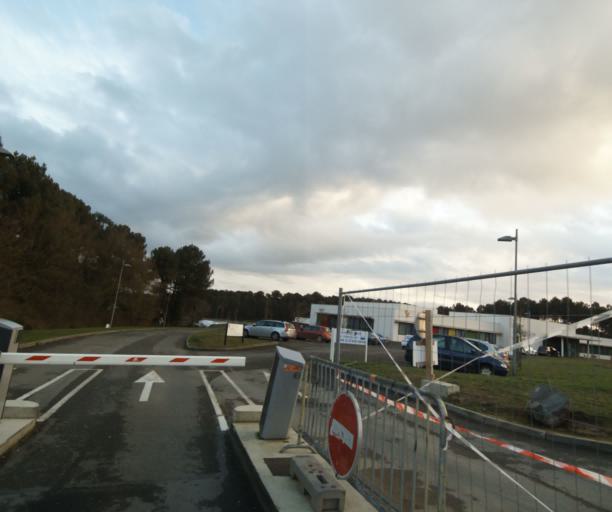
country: FR
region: Pays de la Loire
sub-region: Departement de la Sarthe
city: Le Mans
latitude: 47.9669
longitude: 0.2275
